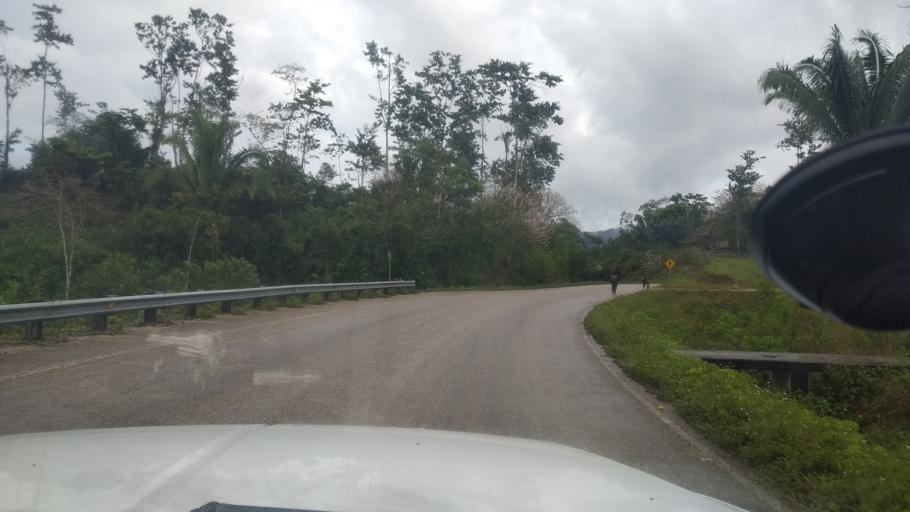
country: GT
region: Peten
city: San Luis
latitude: 16.2018
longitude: -89.1461
